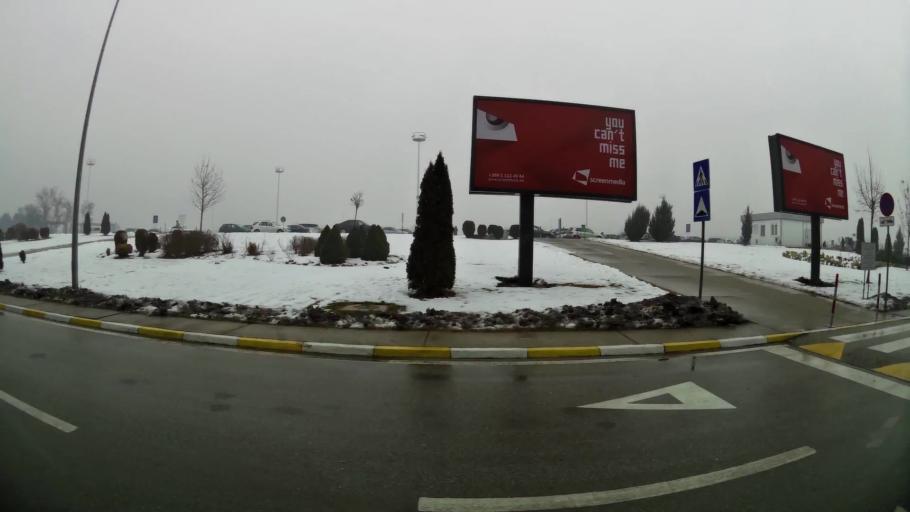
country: MK
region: Petrovec
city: Petrovec
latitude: 41.9614
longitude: 21.6276
